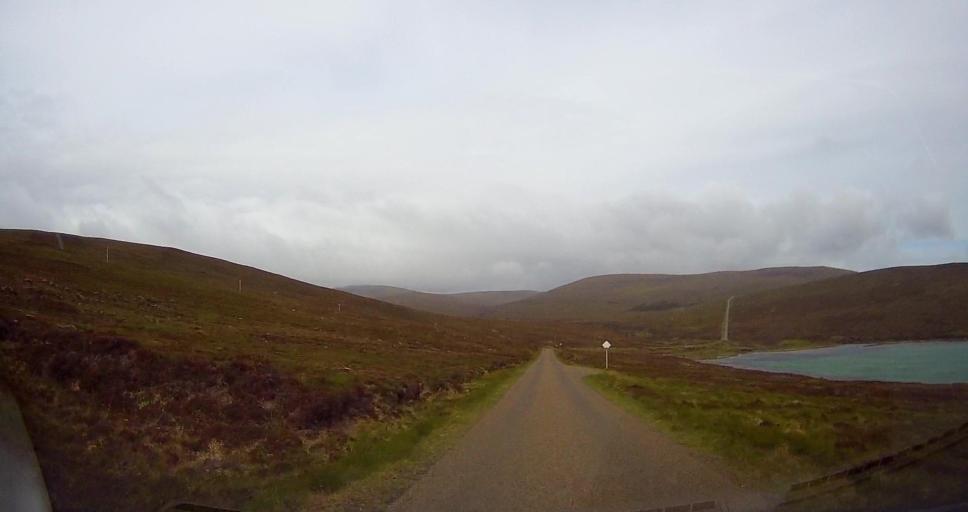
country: GB
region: Scotland
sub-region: Orkney Islands
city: Stromness
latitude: 58.8677
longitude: -3.2231
